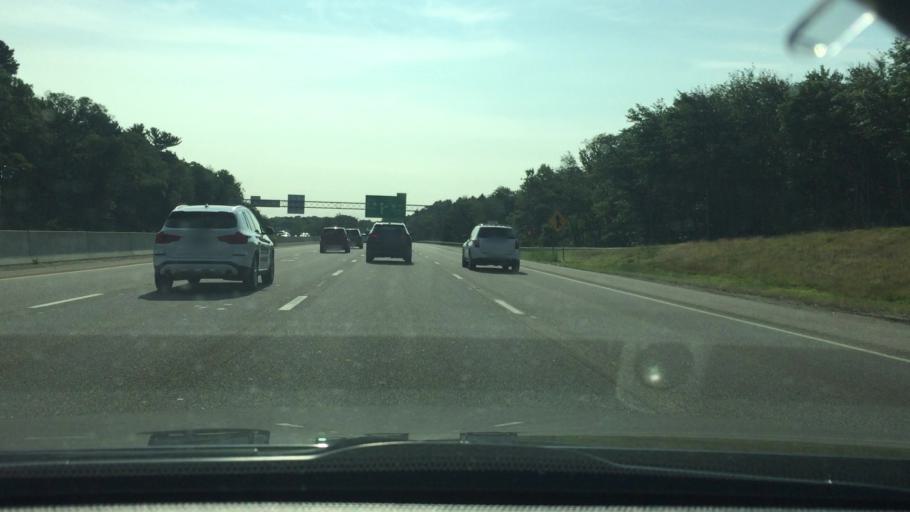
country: US
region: Massachusetts
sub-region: Norfolk County
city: Milton
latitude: 42.2028
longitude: -71.0954
